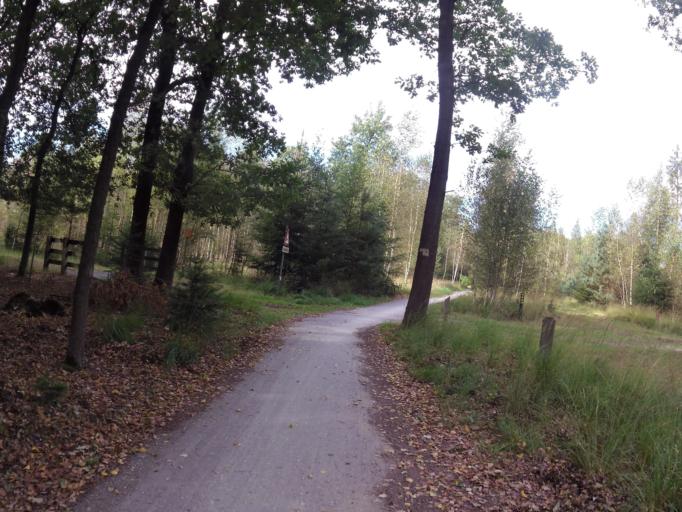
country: NL
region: North Brabant
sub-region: Gemeente Valkenswaard
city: Valkenswaard
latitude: 51.3395
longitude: 5.4958
